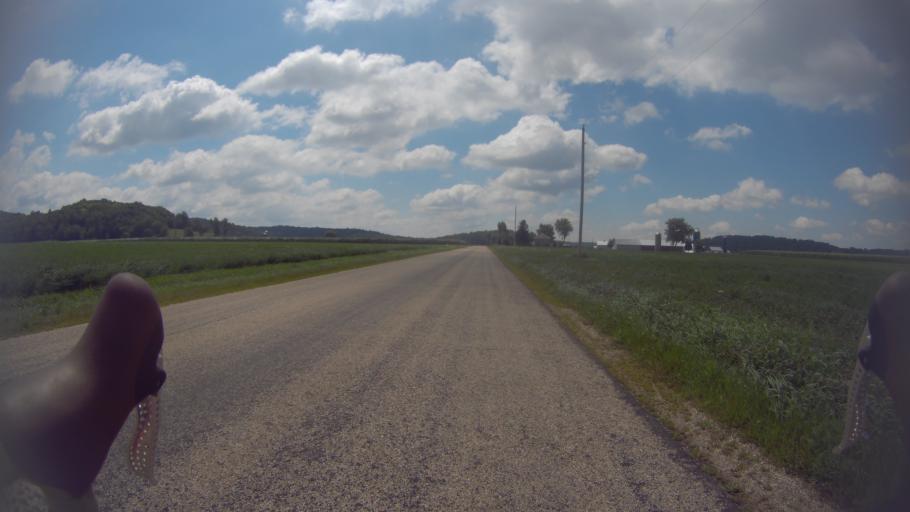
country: US
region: Wisconsin
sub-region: Sauk County
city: Sauk City
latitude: 43.2267
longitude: -89.6404
